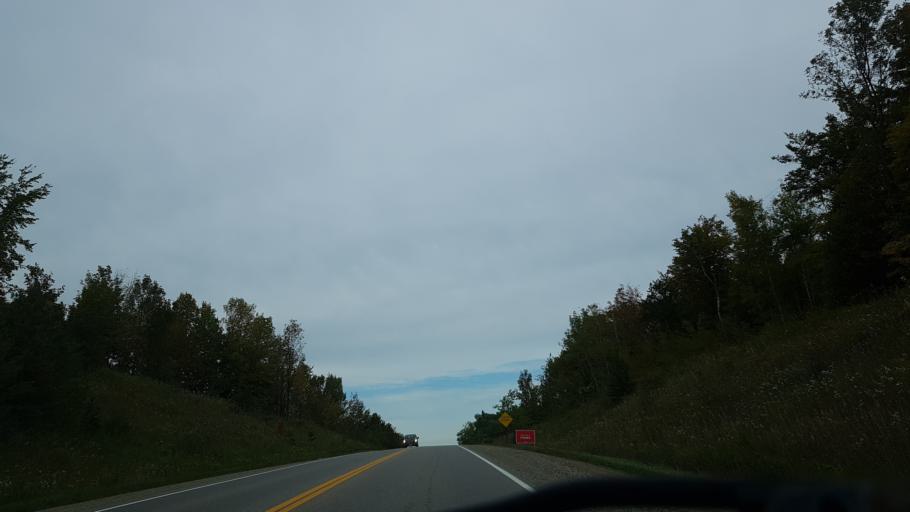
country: CA
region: Ontario
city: Orangeville
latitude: 44.0574
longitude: -80.0132
